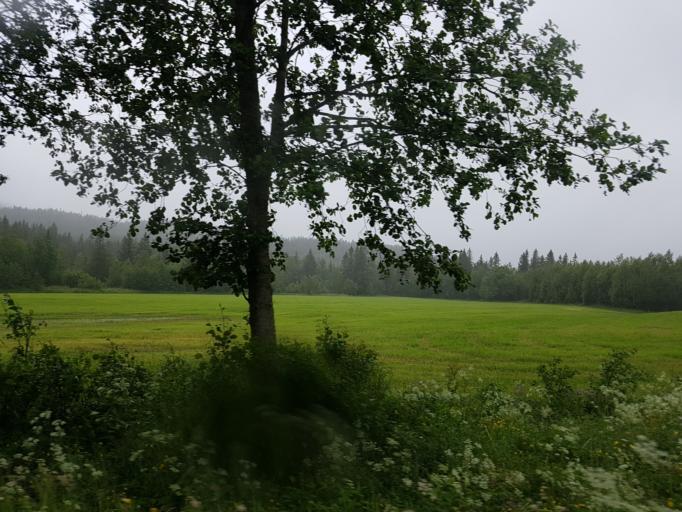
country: NO
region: Sor-Trondelag
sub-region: Selbu
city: Mebonden
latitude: 63.3724
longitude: 11.0735
